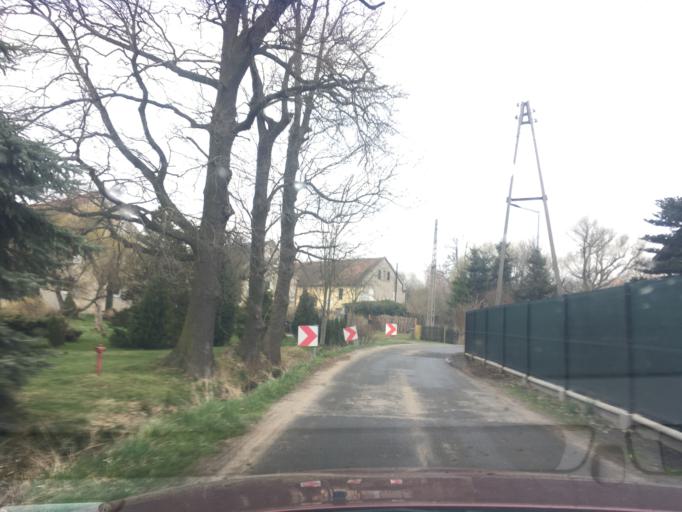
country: PL
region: Lower Silesian Voivodeship
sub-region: Powiat zgorzelecki
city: Lagow
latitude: 51.1764
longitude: 15.0416
